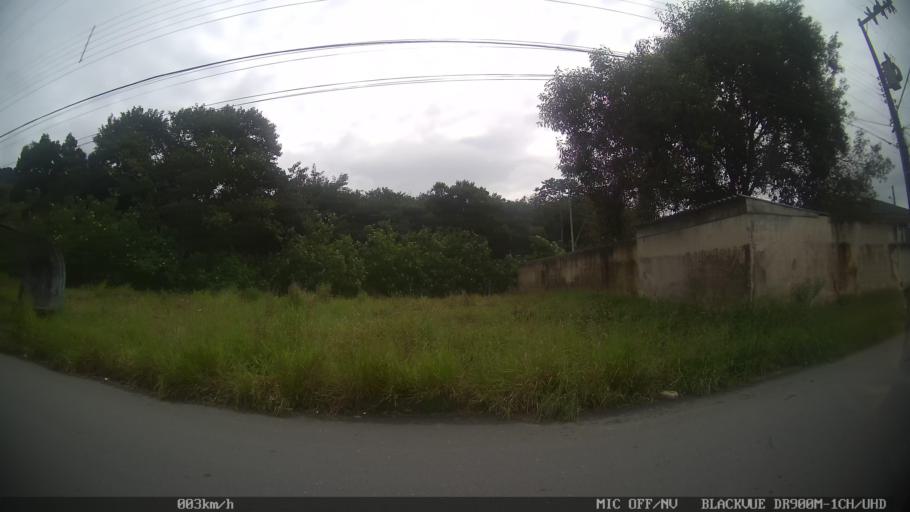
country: BR
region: Santa Catarina
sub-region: Biguacu
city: Biguacu
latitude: -27.5457
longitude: -48.6460
